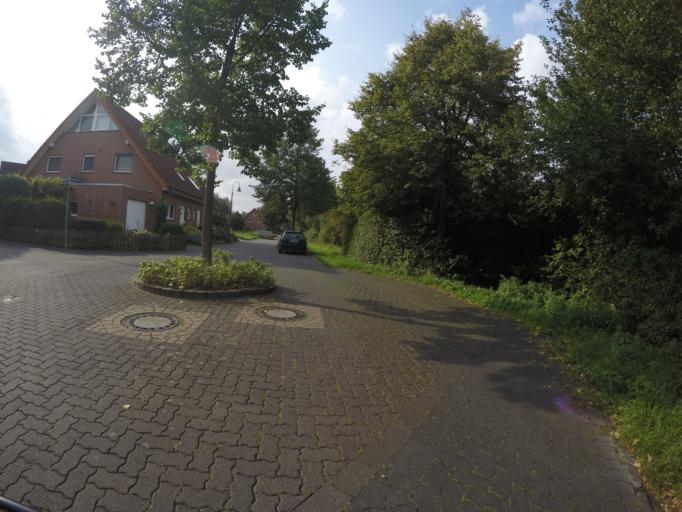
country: DE
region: North Rhine-Westphalia
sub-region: Regierungsbezirk Arnsberg
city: Lippstadt
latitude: 51.6841
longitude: 8.3284
